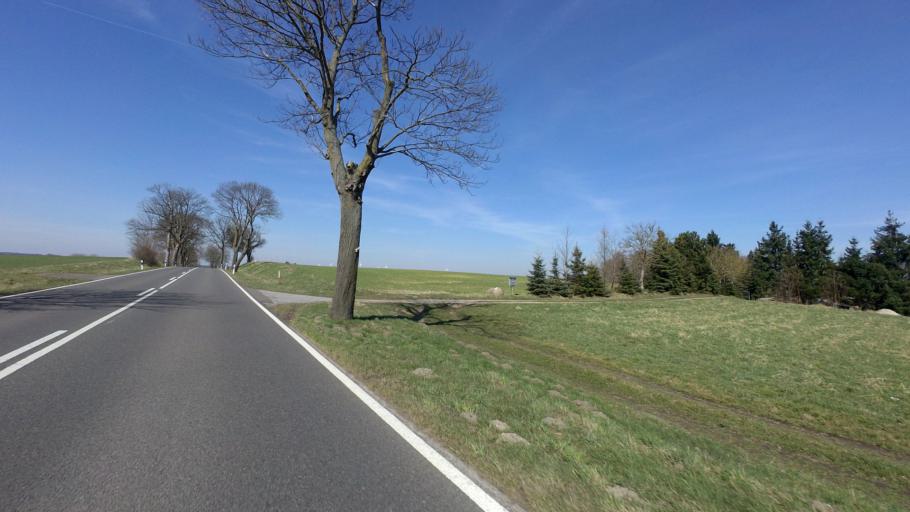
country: DE
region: Brandenburg
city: Protzel
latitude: 52.6151
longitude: 14.0199
